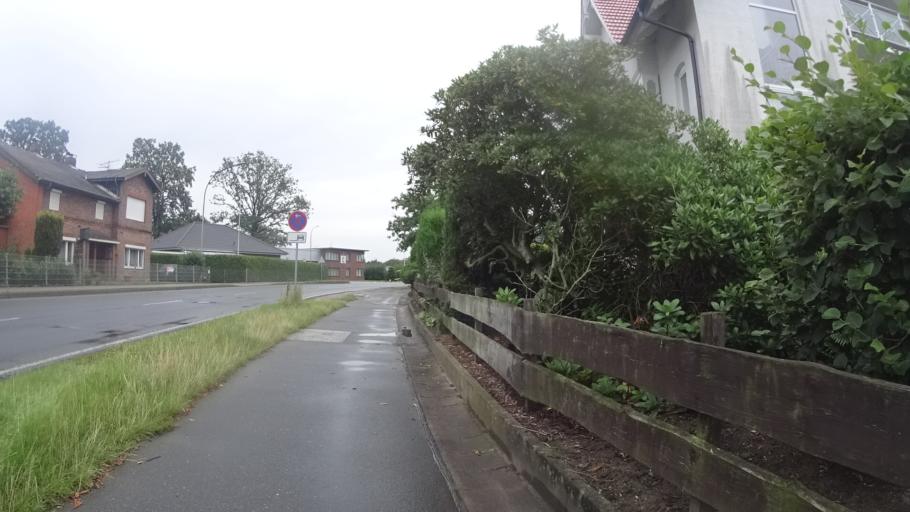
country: DE
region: Schleswig-Holstein
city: Alveslohe
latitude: 53.7891
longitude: 9.9220
